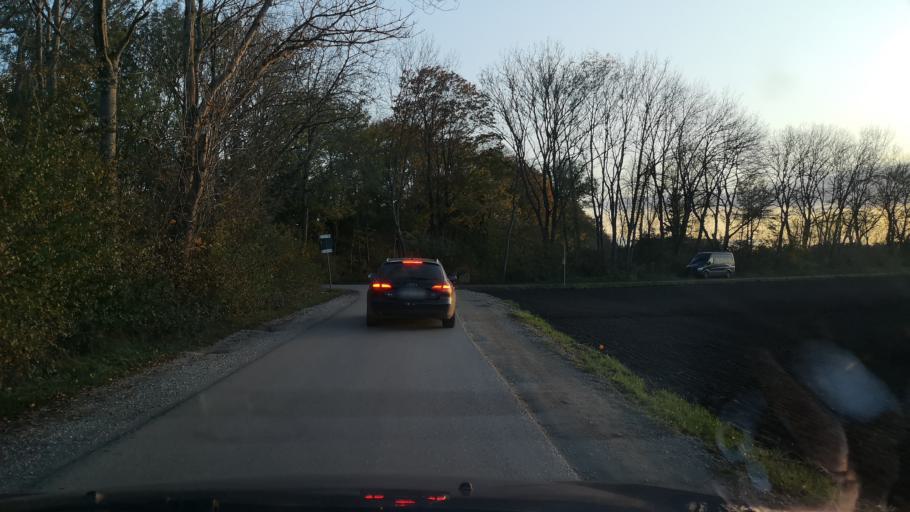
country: DE
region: Bavaria
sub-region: Upper Bavaria
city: Eichenried
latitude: 48.2419
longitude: 11.7500
